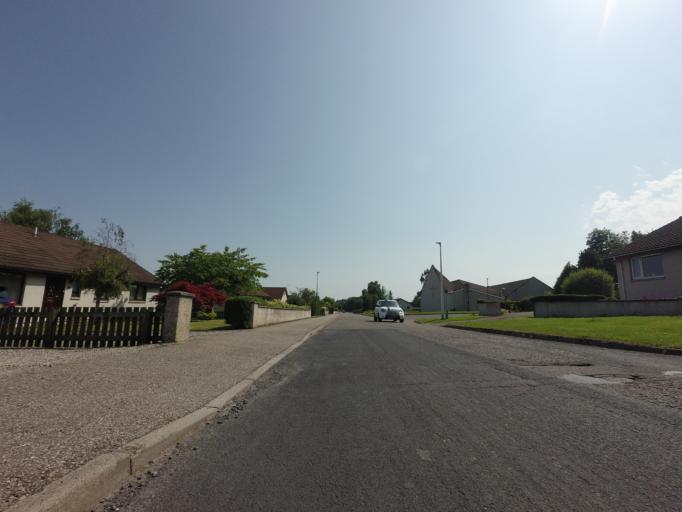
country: GB
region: Scotland
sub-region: Highland
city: Tain
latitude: 57.8054
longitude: -4.0613
